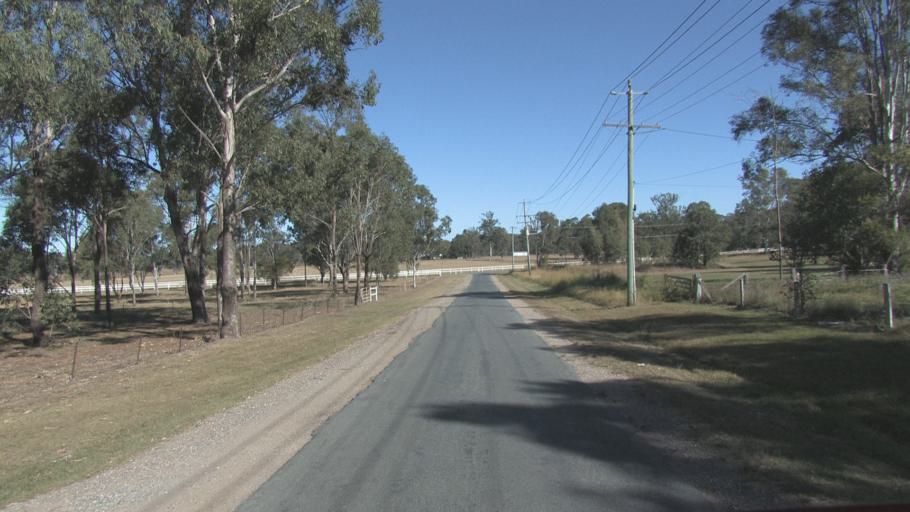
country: AU
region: Queensland
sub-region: Logan
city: North Maclean
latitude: -27.7670
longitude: 153.0234
